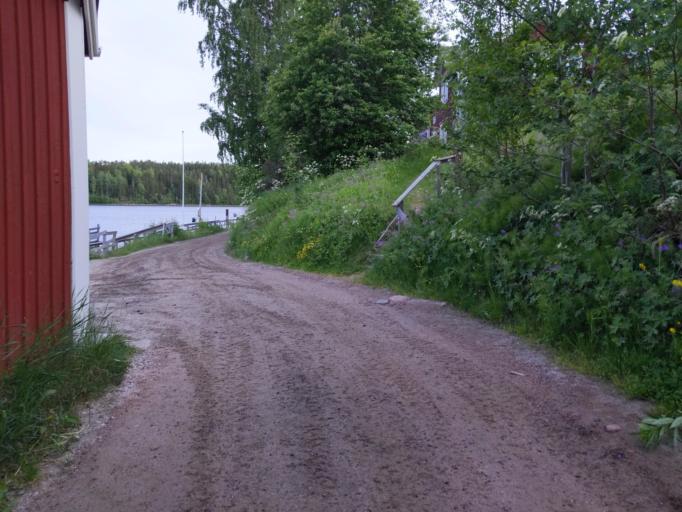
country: SE
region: Vaesternorrland
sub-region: OErnskoeldsviks Kommun
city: Kopmanholmen
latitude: 63.0202
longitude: 18.6463
